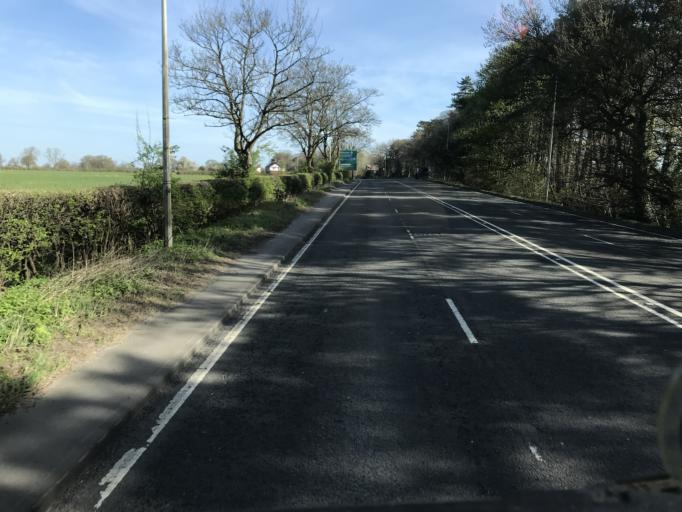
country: GB
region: England
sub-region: Cheshire East
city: Mere
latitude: 53.2973
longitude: -2.4211
